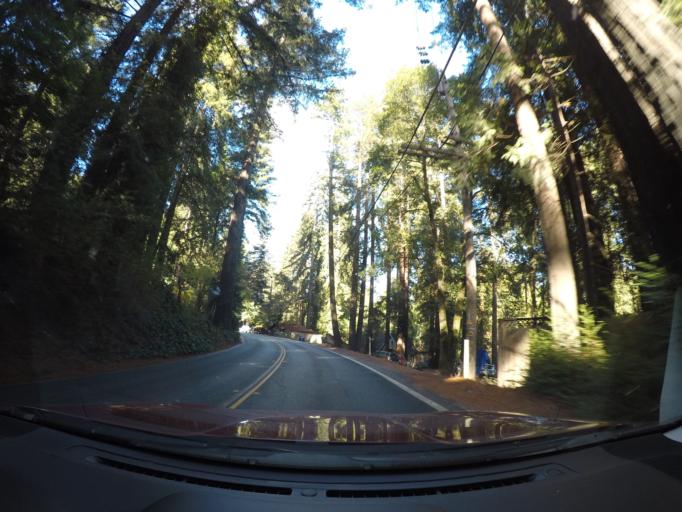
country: US
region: California
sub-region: Santa Cruz County
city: Brookdale
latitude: 37.1124
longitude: -122.1151
